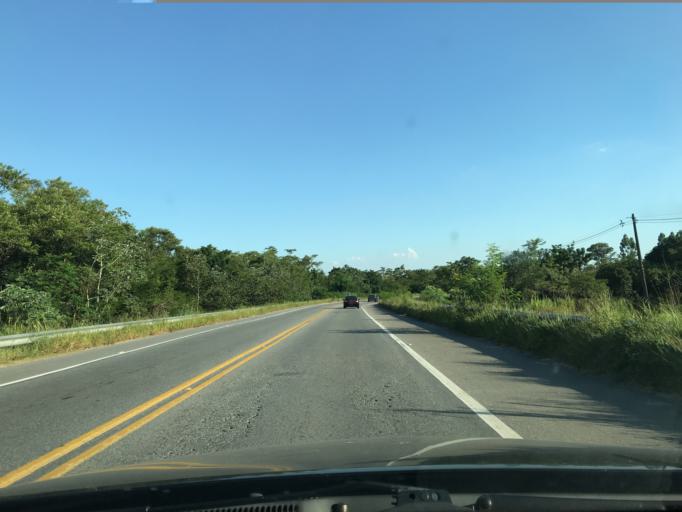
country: BR
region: Sao Paulo
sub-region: Taubate
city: Taubate
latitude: -23.0001
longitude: -45.6401
